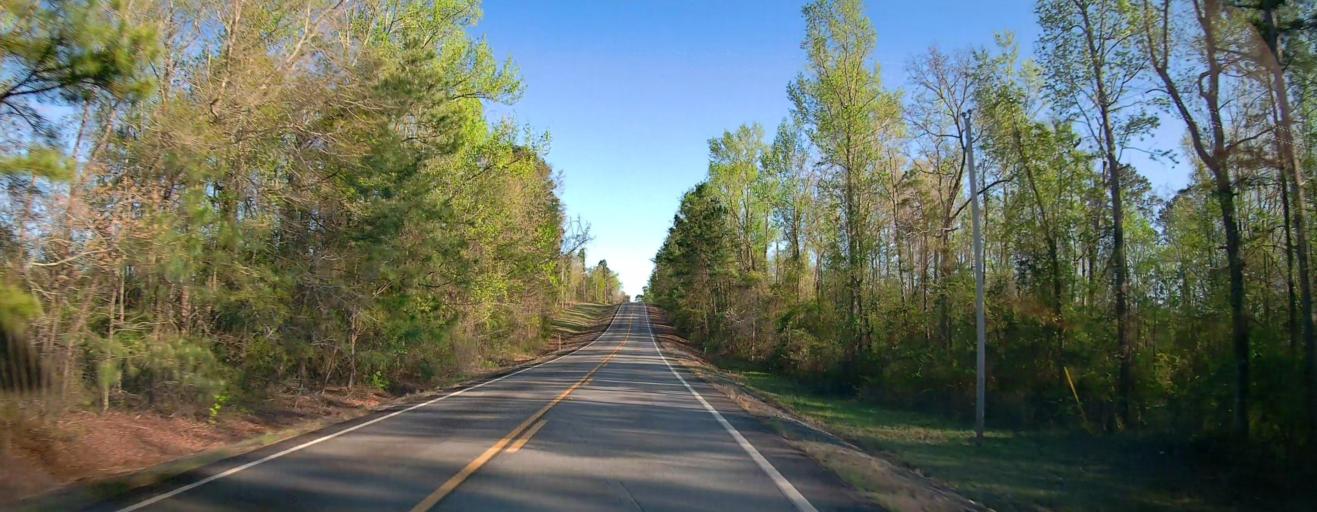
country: US
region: Georgia
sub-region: Wilkinson County
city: Irwinton
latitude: 32.9154
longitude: -83.1272
